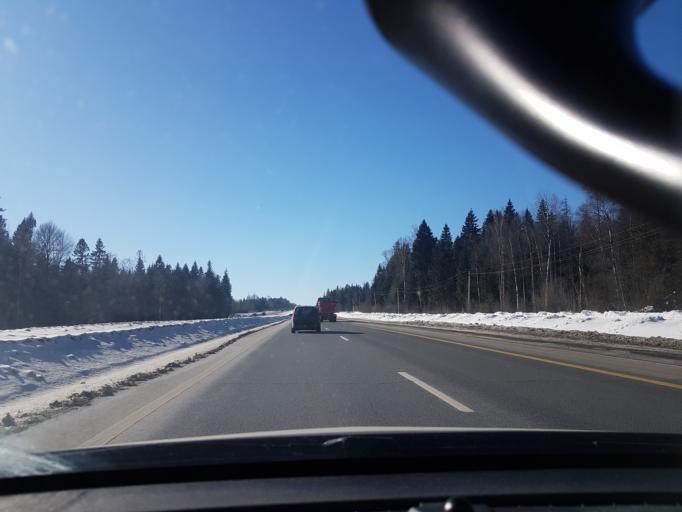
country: RU
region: Moskovskaya
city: Sychevo
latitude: 55.9854
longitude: 36.3272
